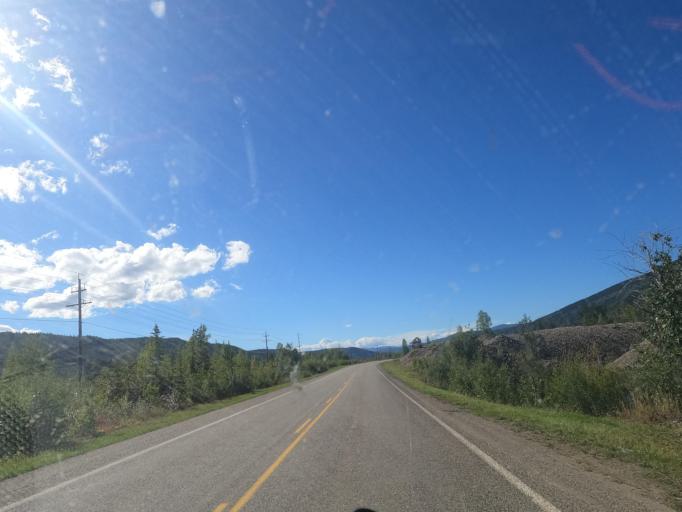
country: CA
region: Yukon
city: Dawson City
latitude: 64.0344
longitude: -139.2804
